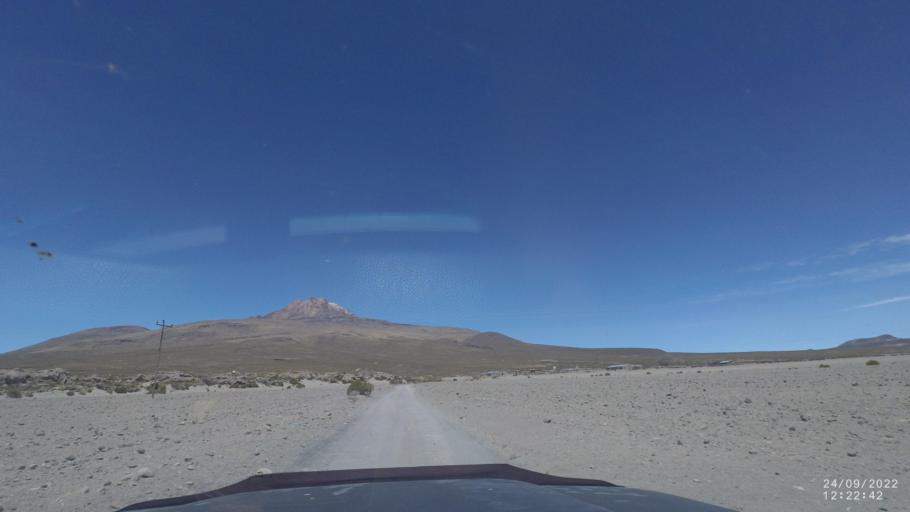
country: BO
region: Potosi
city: Colchani
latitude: -19.7584
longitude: -67.6645
